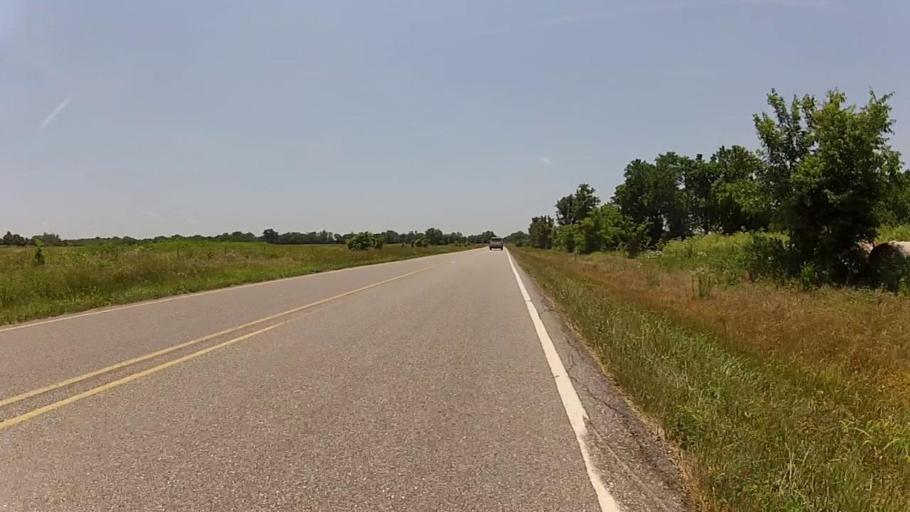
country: US
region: Kansas
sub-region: Montgomery County
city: Cherryvale
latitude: 37.2055
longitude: -95.5388
